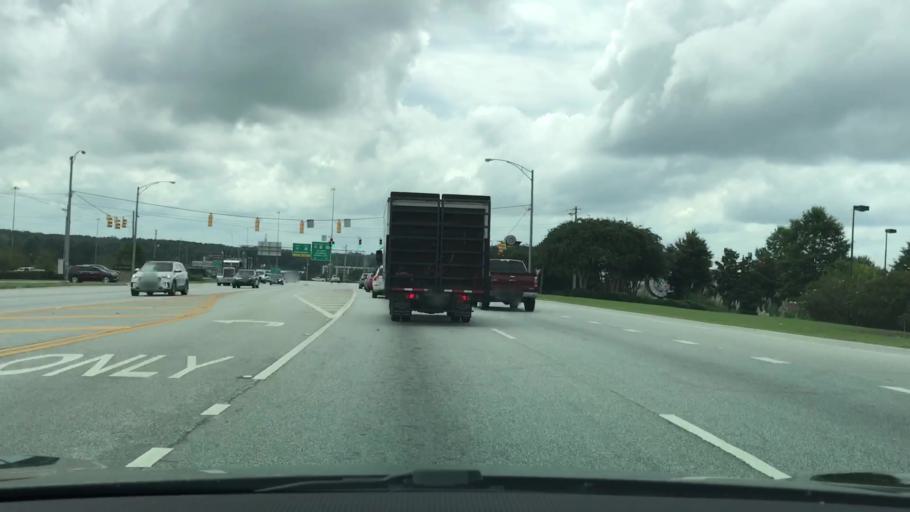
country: US
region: Alabama
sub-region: Lee County
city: Opelika
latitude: 32.6211
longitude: -85.4046
